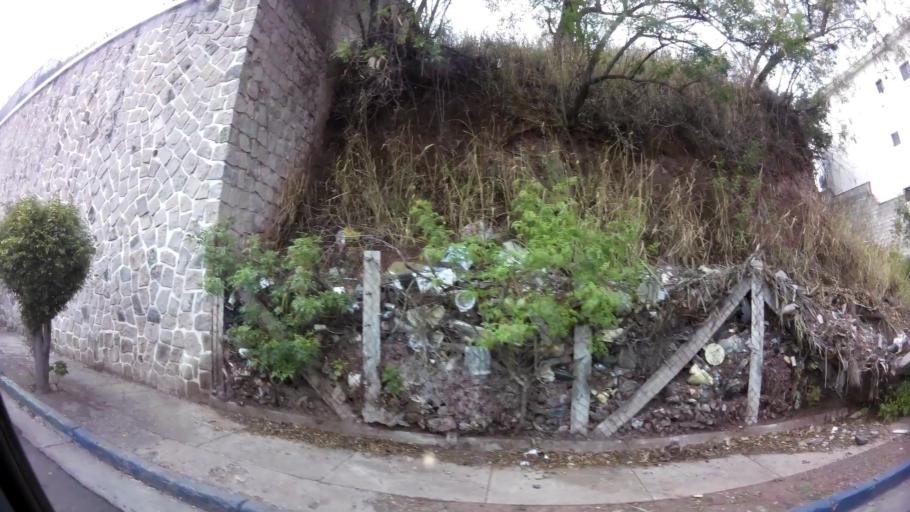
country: HN
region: Francisco Morazan
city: Tegucigalpa
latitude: 14.0968
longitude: -87.1870
